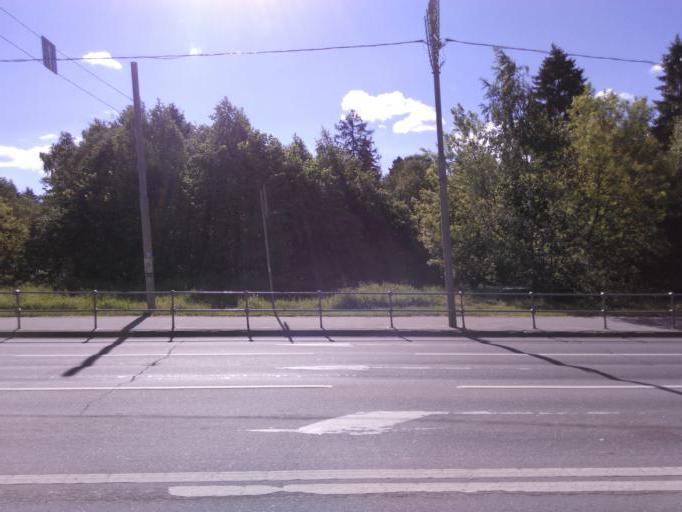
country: RU
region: Moscow
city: Zelenograd
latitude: 55.9914
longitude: 37.1861
